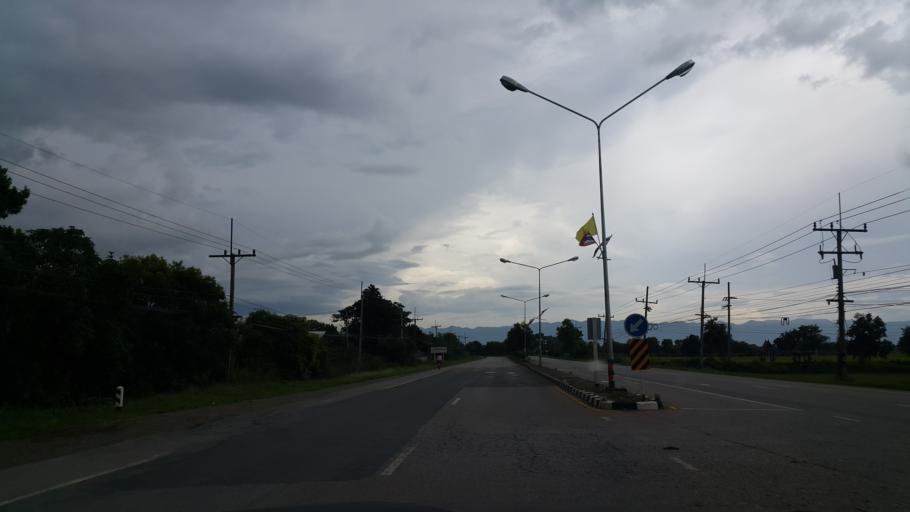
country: TH
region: Phayao
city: Dok Kham Tai
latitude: 19.1558
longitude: 99.9547
